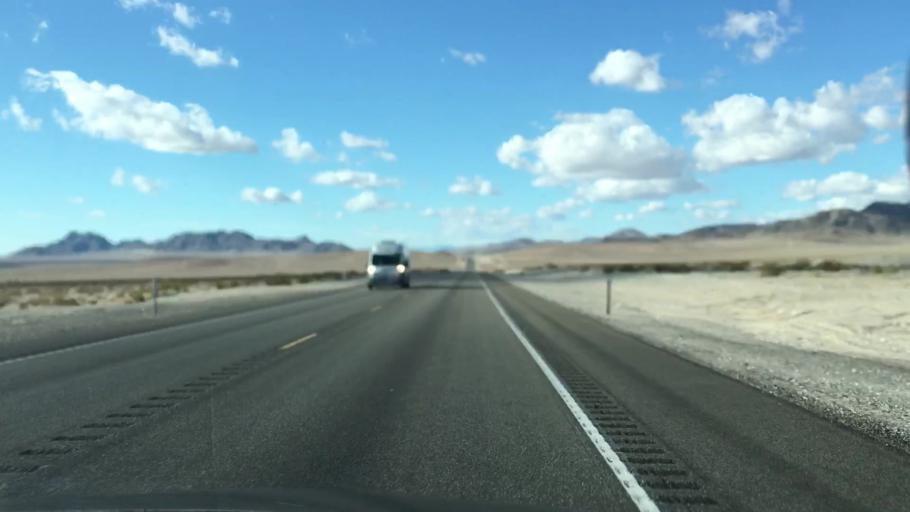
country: US
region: Nevada
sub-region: Nye County
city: Pahrump
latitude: 36.6030
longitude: -116.2534
